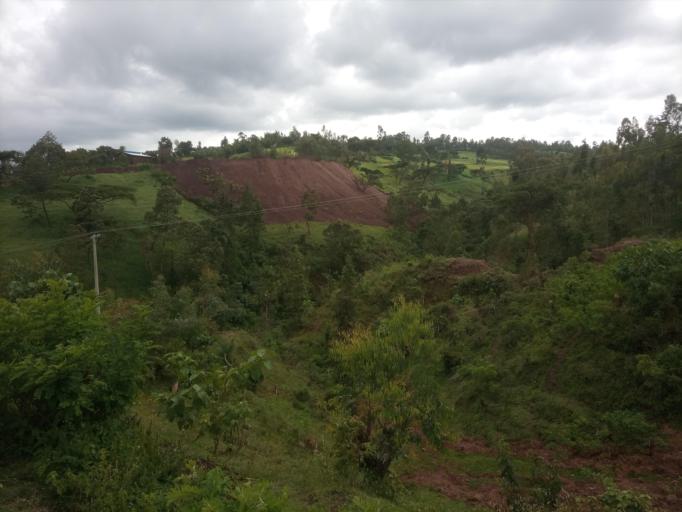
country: ET
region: Southern Nations, Nationalities, and People's Region
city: K'olito
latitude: 7.3754
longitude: 37.8816
